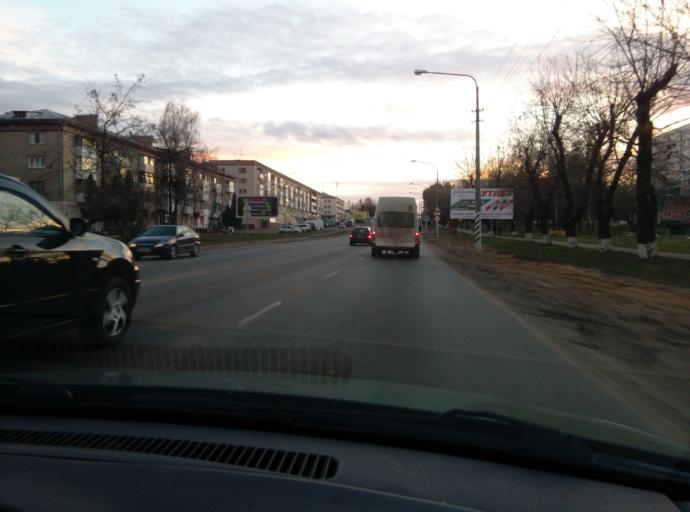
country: BY
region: Minsk
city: Horad Barysaw
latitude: 54.2169
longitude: 28.4900
